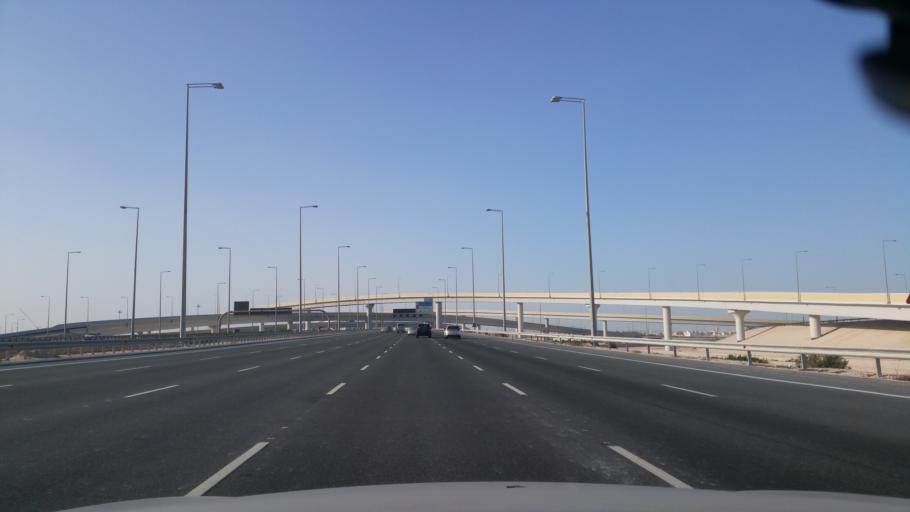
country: QA
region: Al Wakrah
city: Al Wukayr
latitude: 25.1987
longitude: 51.5436
